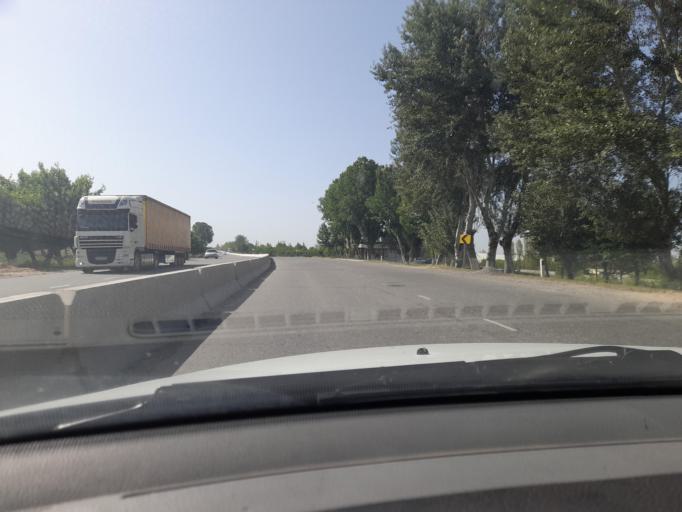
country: UZ
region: Samarqand
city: Chelak
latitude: 39.8319
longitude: 66.8331
